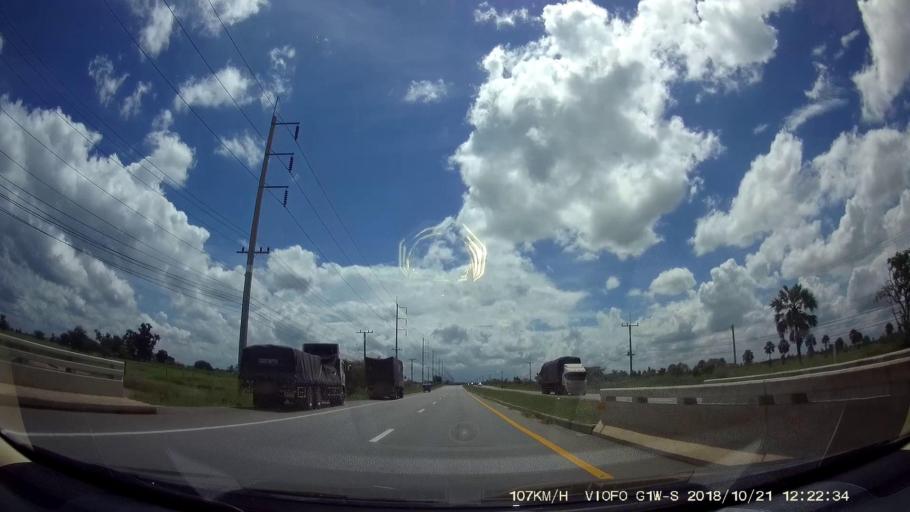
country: TH
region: Nakhon Ratchasima
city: Dan Khun Thot
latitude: 15.2590
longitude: 101.7895
